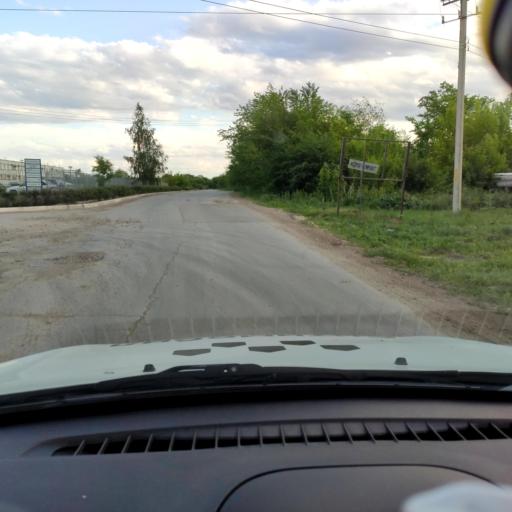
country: RU
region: Samara
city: Podstepki
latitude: 53.5801
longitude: 49.2287
